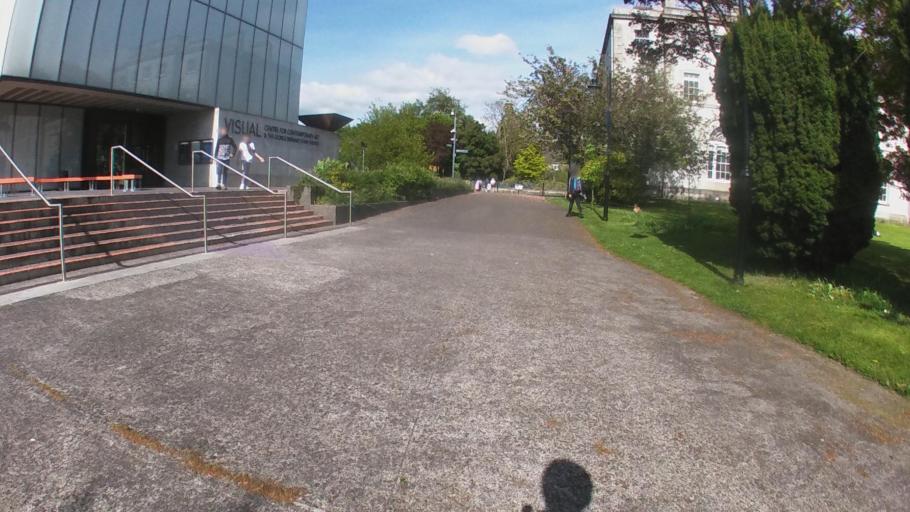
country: IE
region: Leinster
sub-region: County Carlow
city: Carlow
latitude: 52.8378
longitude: -6.9278
